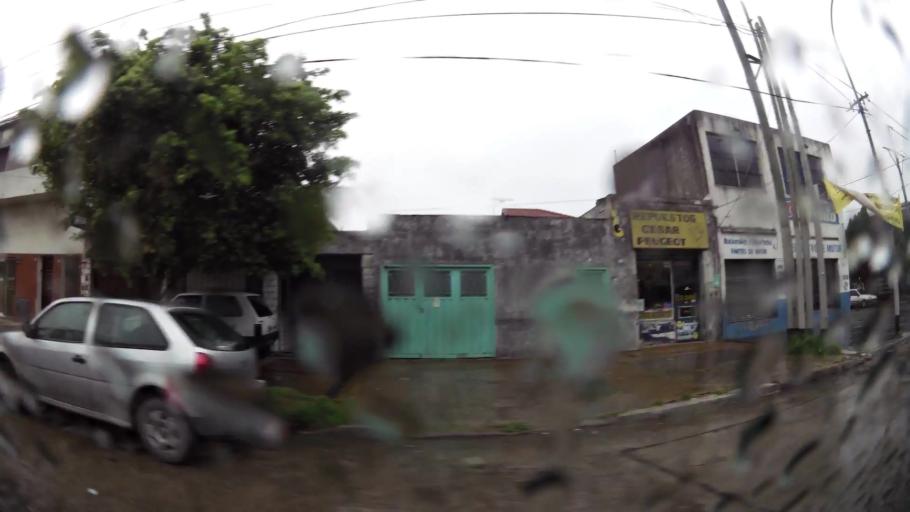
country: AR
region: Buenos Aires
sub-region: Partido de Lanus
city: Lanus
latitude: -34.7001
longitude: -58.4118
